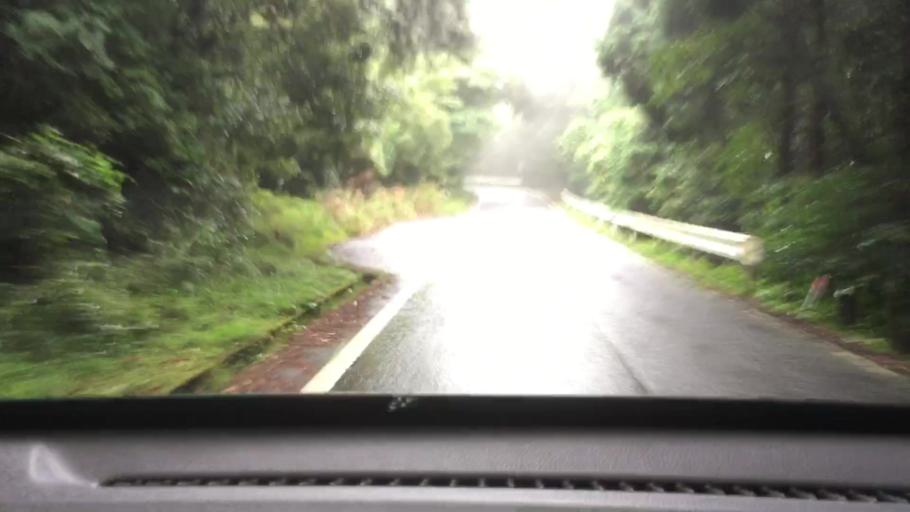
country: JP
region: Nagasaki
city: Togitsu
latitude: 32.9160
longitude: 129.7313
